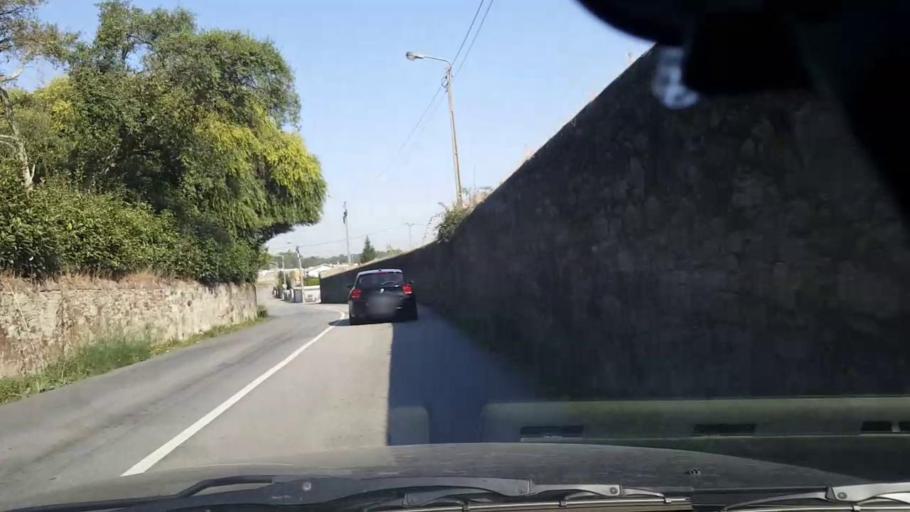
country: PT
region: Porto
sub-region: Vila do Conde
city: Arvore
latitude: 41.3316
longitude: -8.6807
